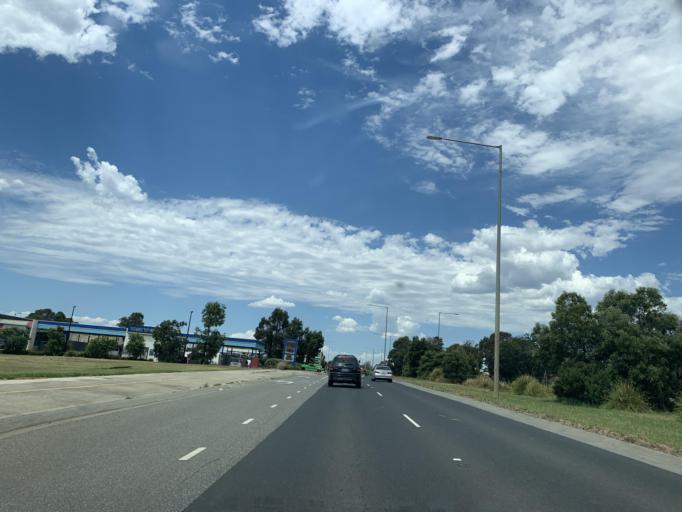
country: AU
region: Victoria
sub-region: Casey
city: Cranbourne West
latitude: -38.1104
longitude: 145.2622
